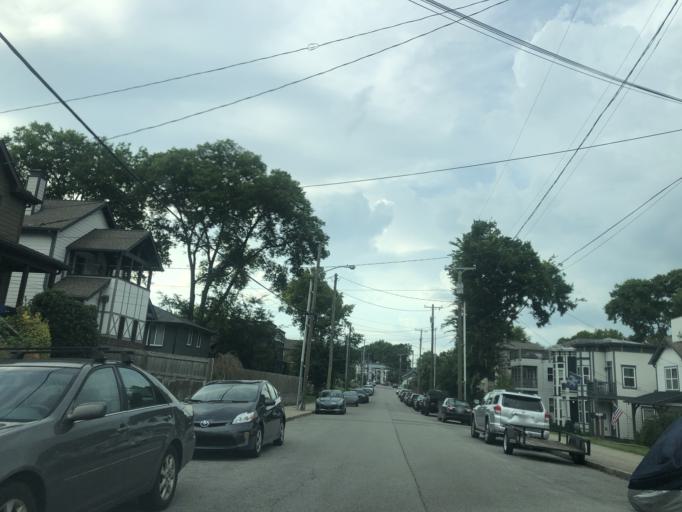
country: US
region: Tennessee
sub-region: Davidson County
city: Nashville
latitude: 36.1820
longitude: -86.7941
